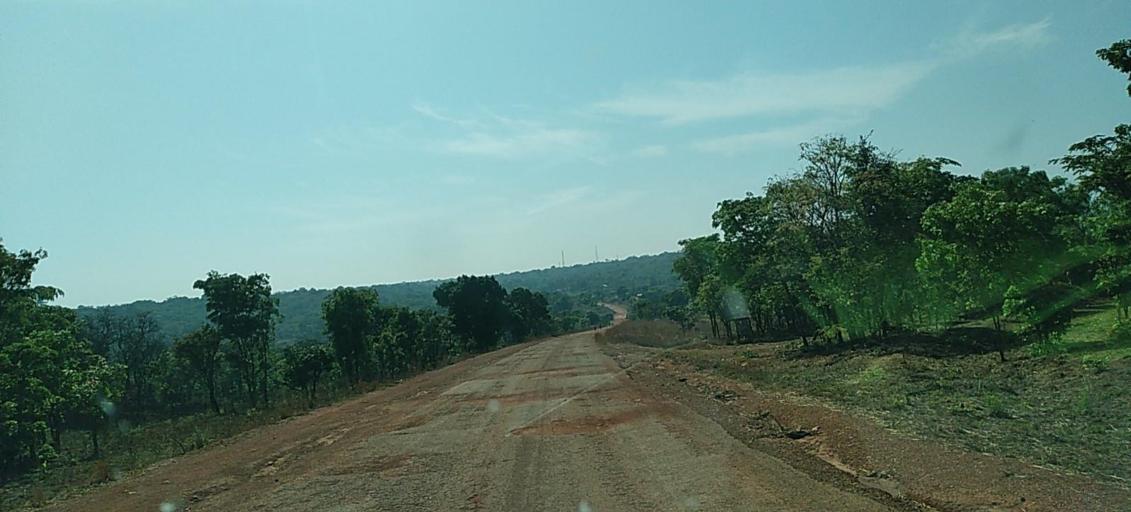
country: ZM
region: North-Western
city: Mwinilunga
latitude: -11.8237
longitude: 25.1203
